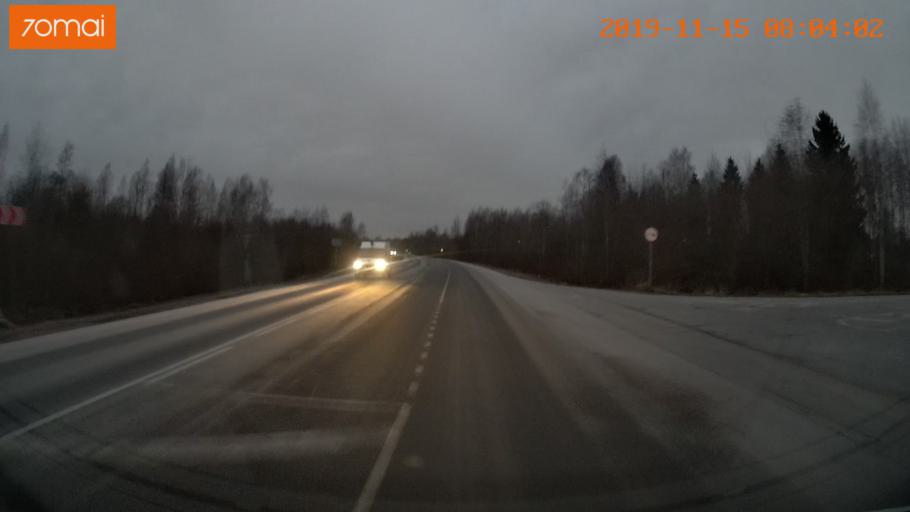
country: RU
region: Vologda
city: Cherepovets
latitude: 59.0039
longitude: 38.0823
